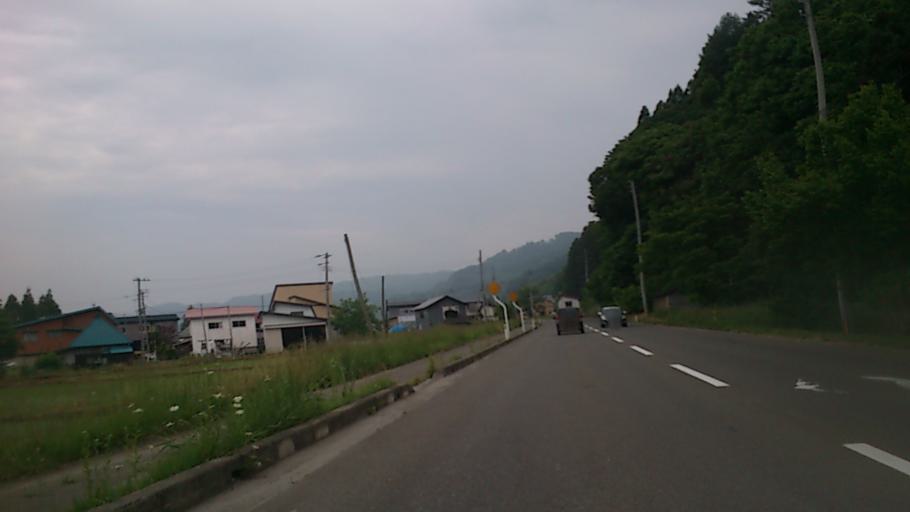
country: JP
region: Aomori
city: Hirosaki
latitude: 40.5904
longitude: 140.3323
